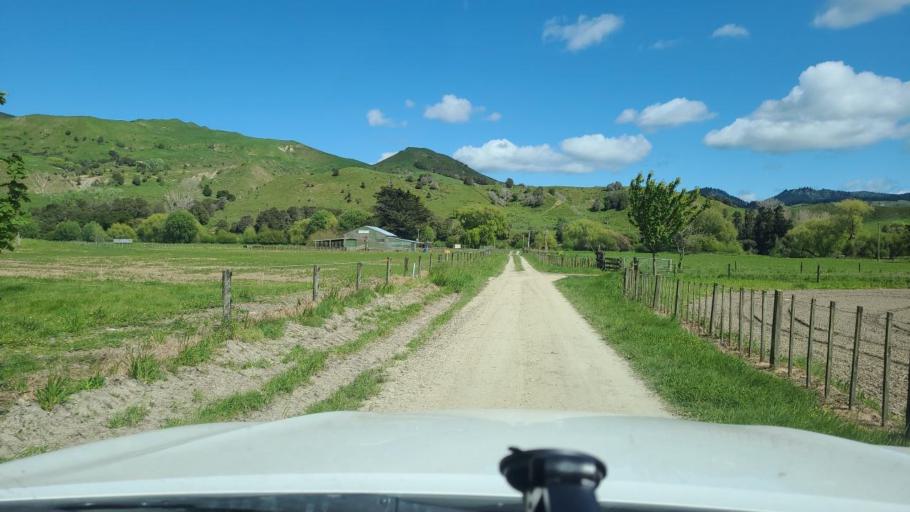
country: NZ
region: Gisborne
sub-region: Gisborne District
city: Gisborne
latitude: -38.7391
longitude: 177.8289
